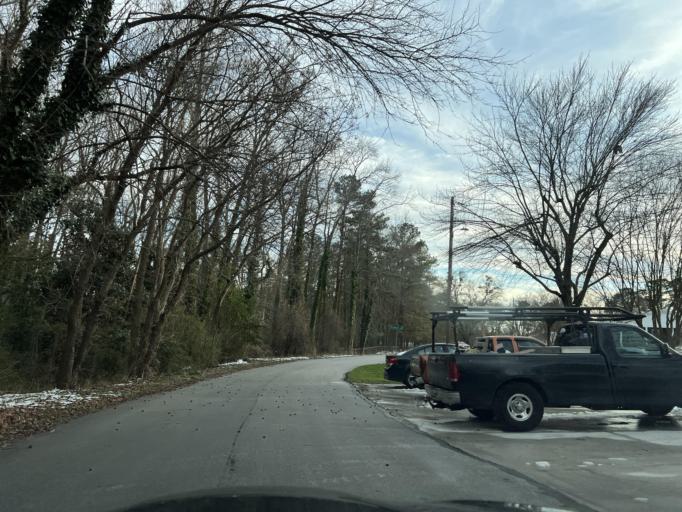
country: US
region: North Carolina
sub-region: Wake County
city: Raleigh
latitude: 35.8046
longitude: -78.5795
